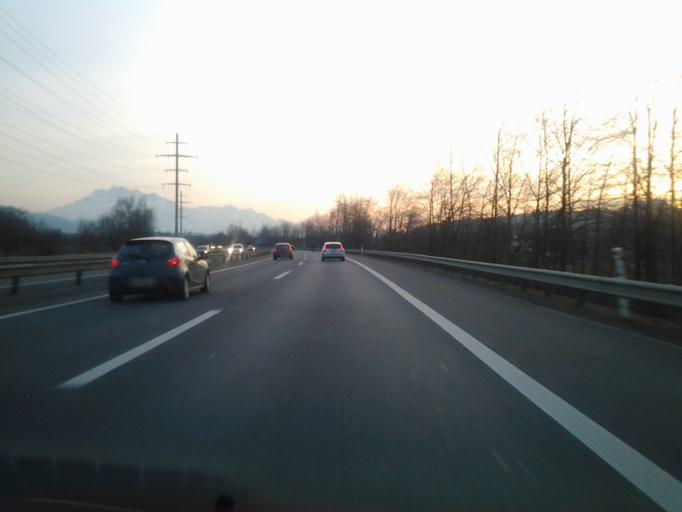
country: CH
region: Lucerne
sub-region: Lucerne-Land District
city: Root
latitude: 47.1372
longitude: 8.4028
